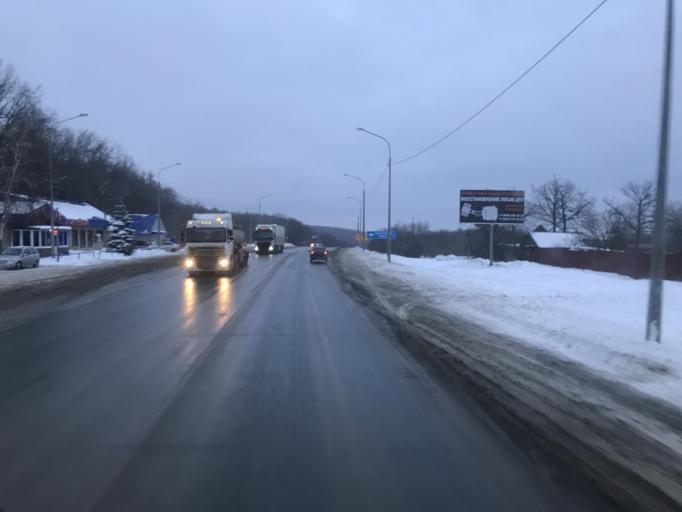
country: RU
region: Samara
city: Zhigulevsk
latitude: 53.3854
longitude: 49.4558
